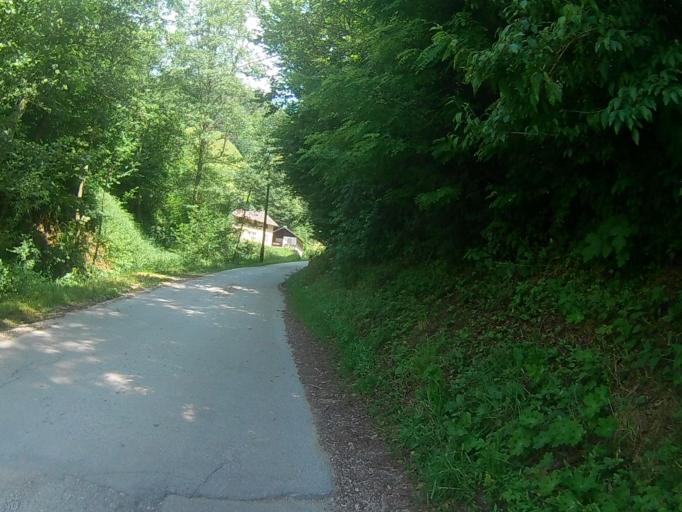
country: SI
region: Maribor
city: Bresternica
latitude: 46.5765
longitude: 15.5804
